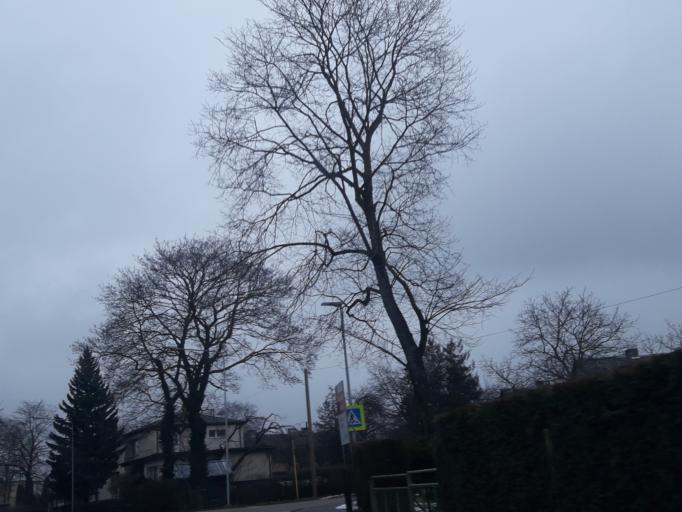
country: EE
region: Saare
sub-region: Kuressaare linn
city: Kuressaare
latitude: 58.2528
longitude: 22.4761
